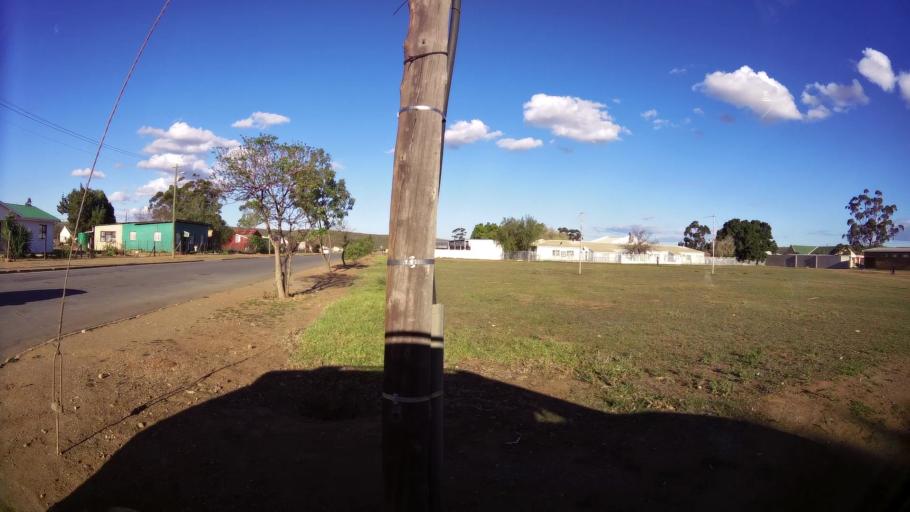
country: ZA
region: Western Cape
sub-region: Eden District Municipality
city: Riversdale
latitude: -34.1012
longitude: 20.9618
